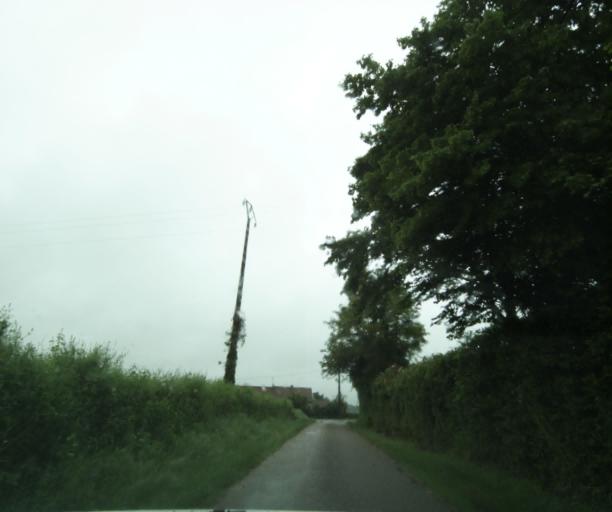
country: FR
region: Bourgogne
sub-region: Departement de Saone-et-Loire
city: Charolles
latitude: 46.4118
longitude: 4.3238
